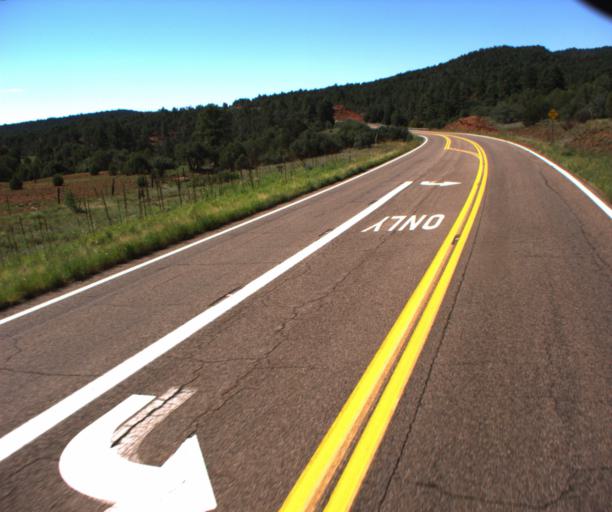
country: US
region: Arizona
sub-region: Navajo County
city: Cibecue
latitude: 33.9567
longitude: -110.3312
